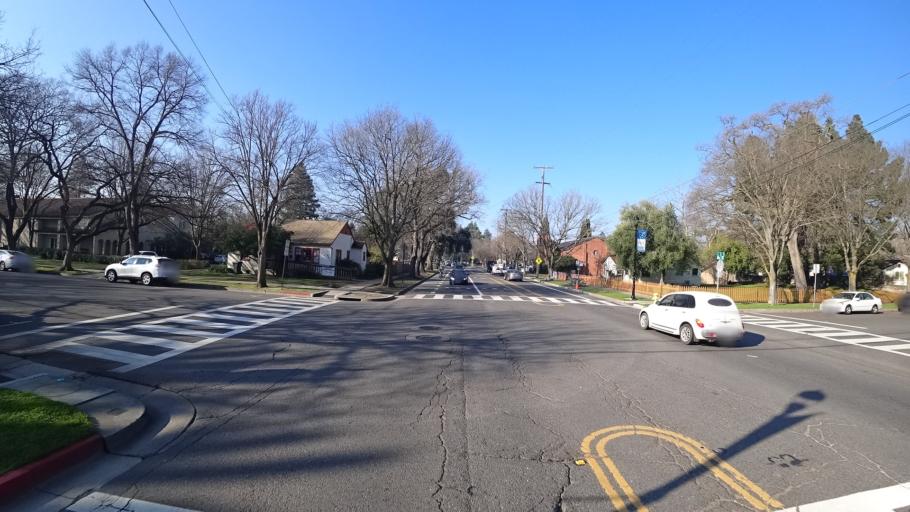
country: US
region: California
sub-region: Yolo County
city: Davis
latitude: 38.5469
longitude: -121.7432
